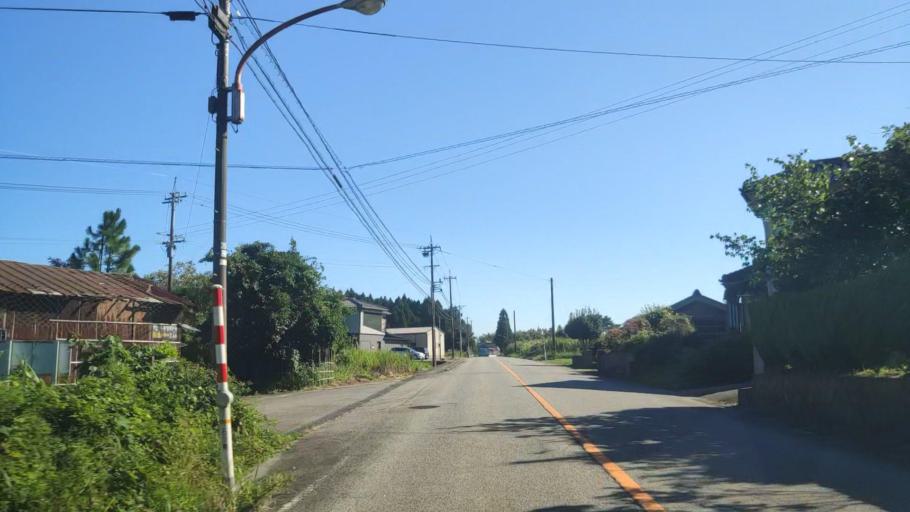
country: JP
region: Ishikawa
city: Nanao
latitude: 37.2603
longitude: 137.0889
